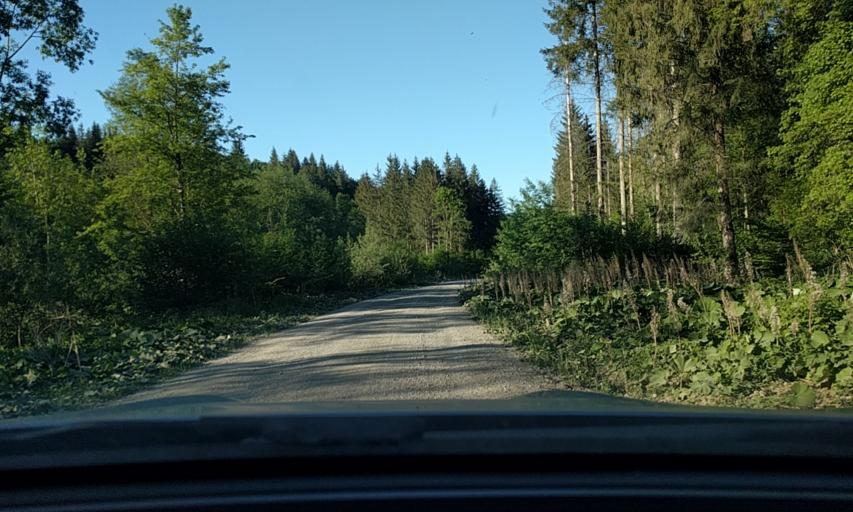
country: RO
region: Bacau
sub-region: Comuna Oituz
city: Ferestrau-Oituz
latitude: 46.1644
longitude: 26.5668
